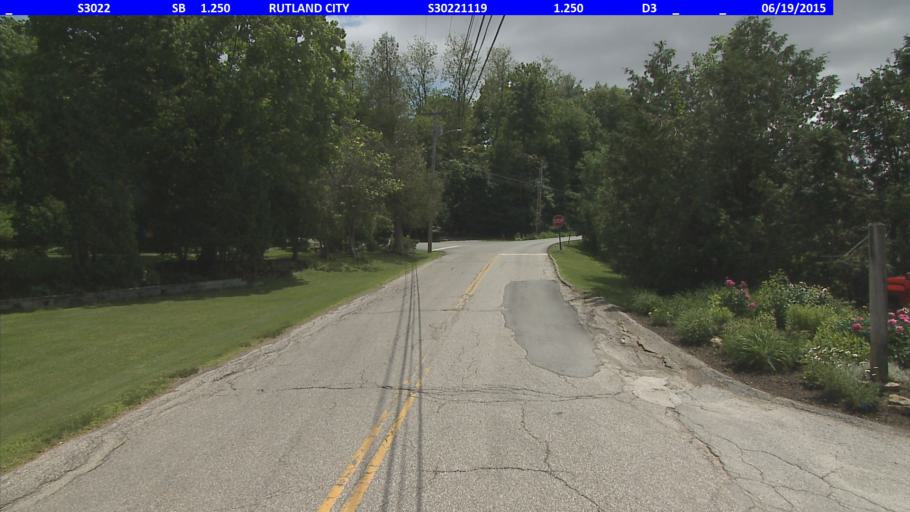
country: US
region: Vermont
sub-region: Rutland County
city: Rutland
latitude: 43.6264
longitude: -72.9863
